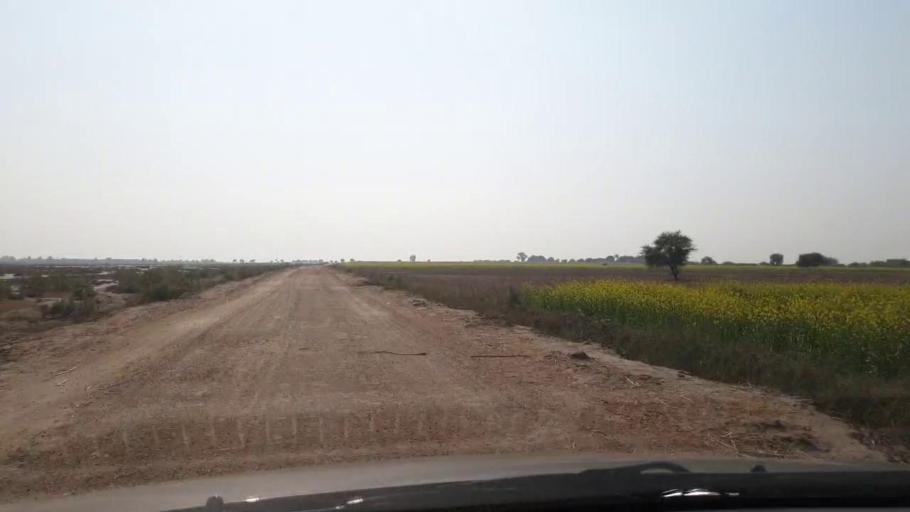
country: PK
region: Sindh
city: Jhol
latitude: 25.8719
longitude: 68.9978
